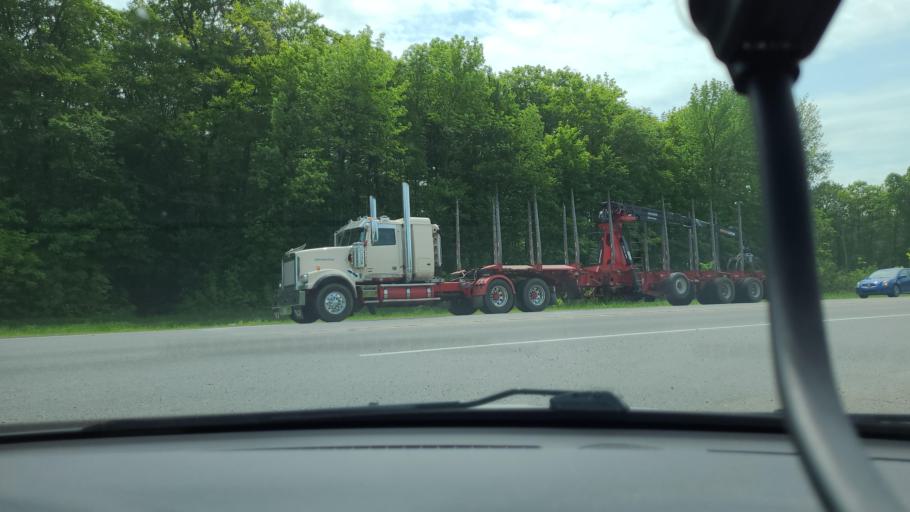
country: CA
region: Quebec
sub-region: Lanaudiere
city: Crabtree
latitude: 45.9688
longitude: -73.4933
